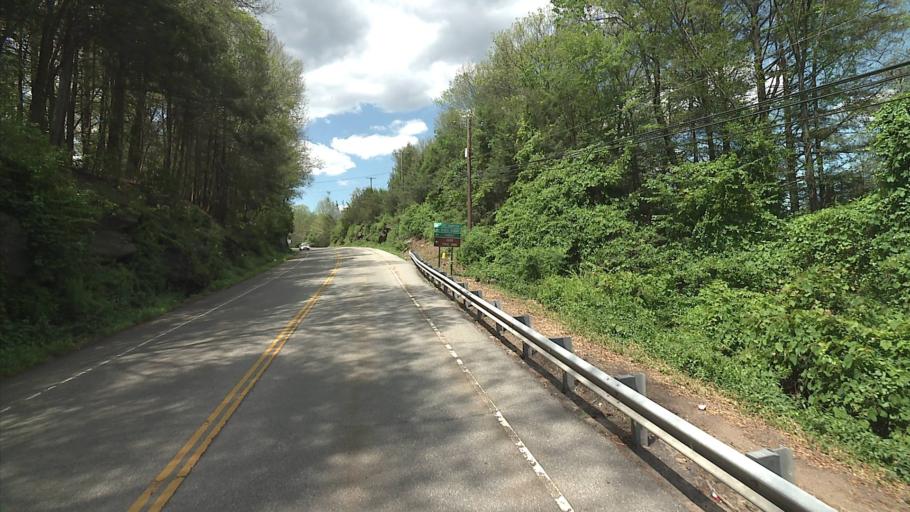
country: US
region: Connecticut
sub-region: Middlesex County
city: Moodus
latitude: 41.5160
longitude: -72.4840
